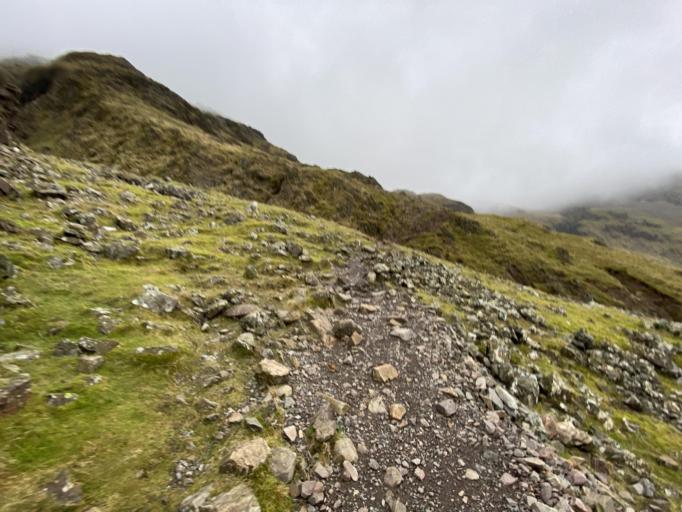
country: GB
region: England
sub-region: Cumbria
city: Keswick
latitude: 54.4718
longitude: -3.2034
